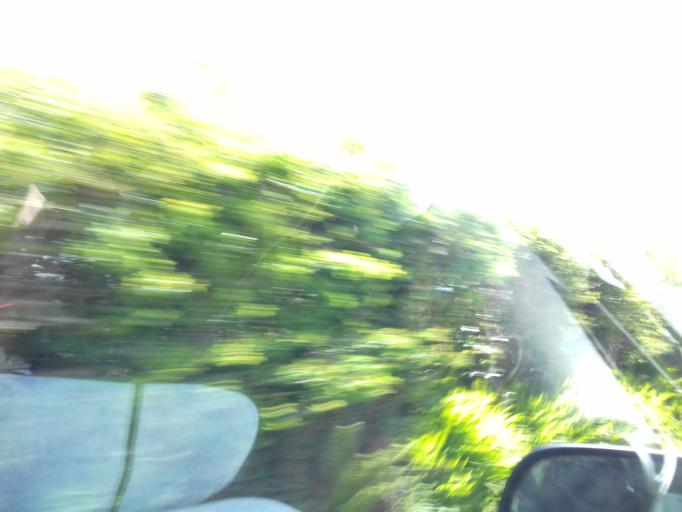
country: IE
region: Munster
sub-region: Waterford
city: Dunmore East
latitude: 52.2441
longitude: -6.8600
